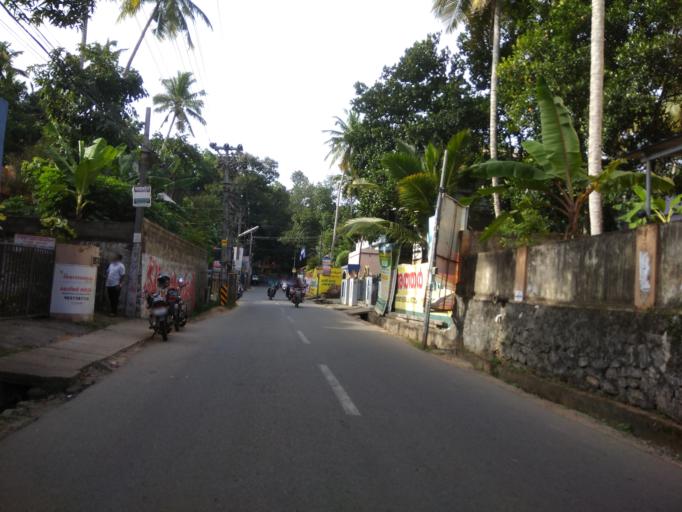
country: IN
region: Kerala
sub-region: Thiruvananthapuram
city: Thiruvananthapuram
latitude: 8.4563
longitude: 77.0003
